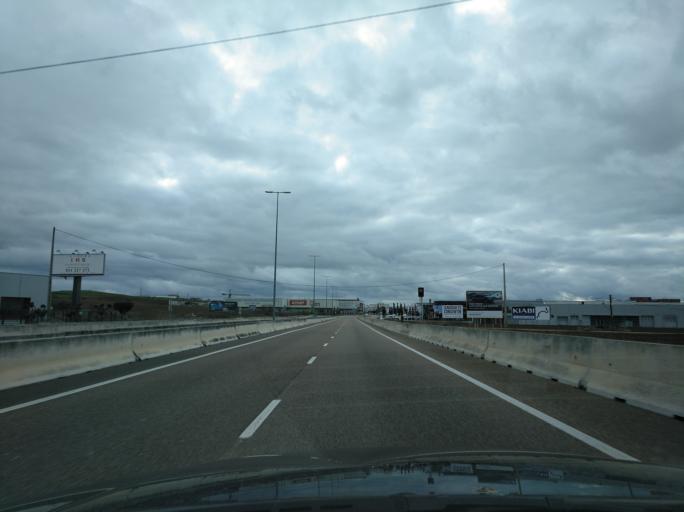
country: ES
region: Extremadura
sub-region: Provincia de Badajoz
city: Badajoz
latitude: 38.8814
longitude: -6.9385
